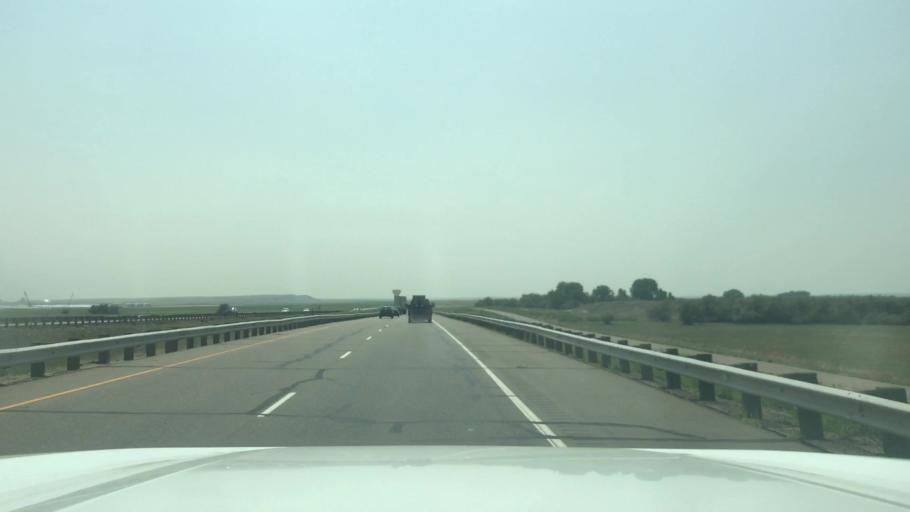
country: US
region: Colorado
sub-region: Pueblo County
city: Pueblo
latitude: 38.1832
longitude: -104.6339
